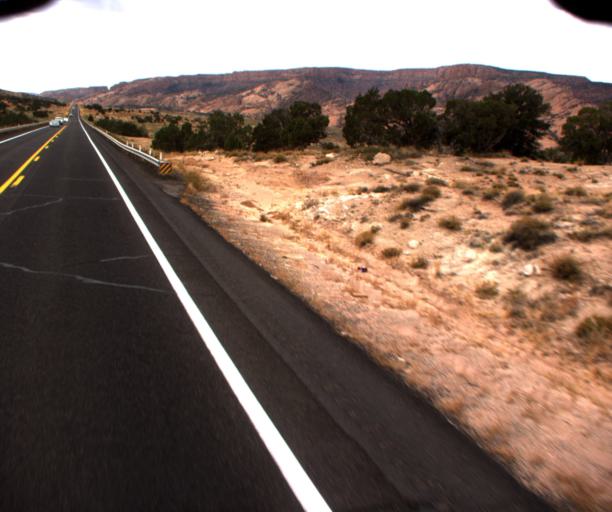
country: US
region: Arizona
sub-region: Navajo County
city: Kayenta
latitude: 36.6832
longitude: -110.3820
